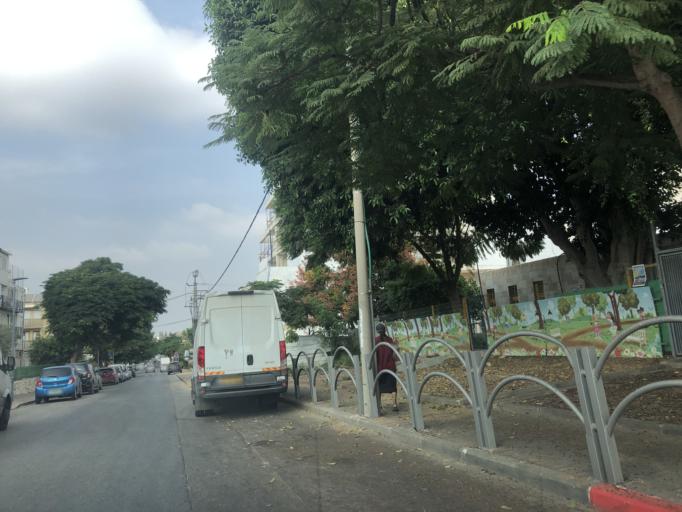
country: IL
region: Central District
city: Rosh Ha'Ayin
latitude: 32.0948
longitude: 34.9524
